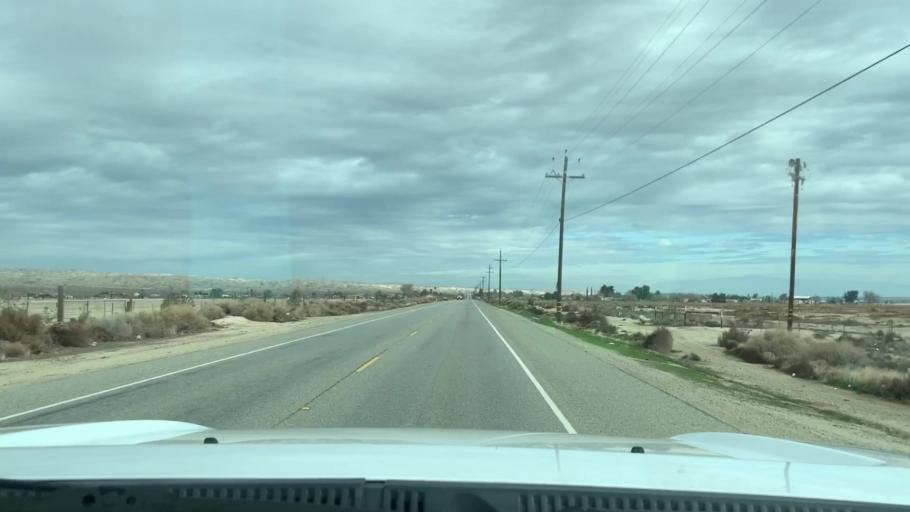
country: US
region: California
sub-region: Kern County
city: Ford City
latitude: 35.2134
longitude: -119.4004
